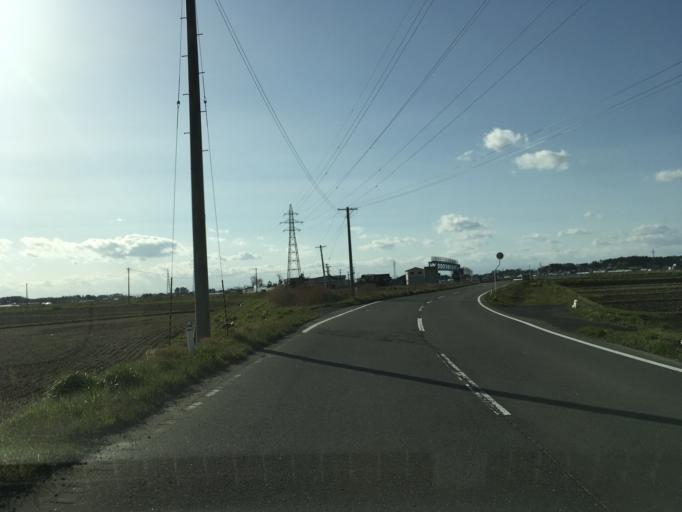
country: JP
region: Miyagi
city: Wakuya
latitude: 38.6568
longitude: 141.2340
